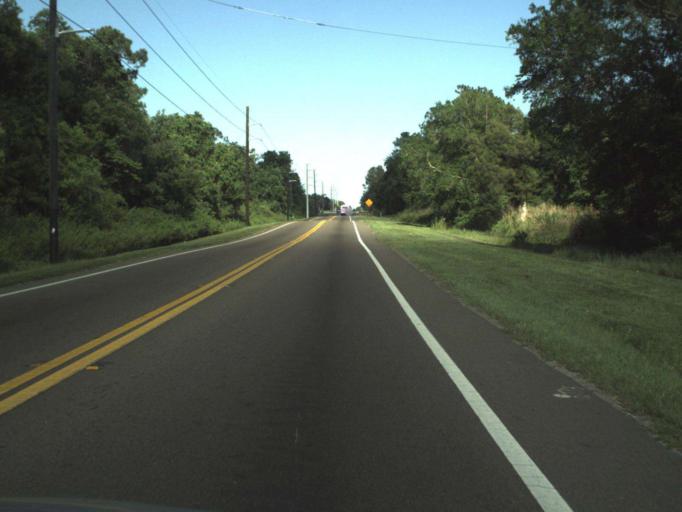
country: US
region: Florida
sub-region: Seminole County
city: Midway
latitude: 28.7868
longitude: -81.2501
